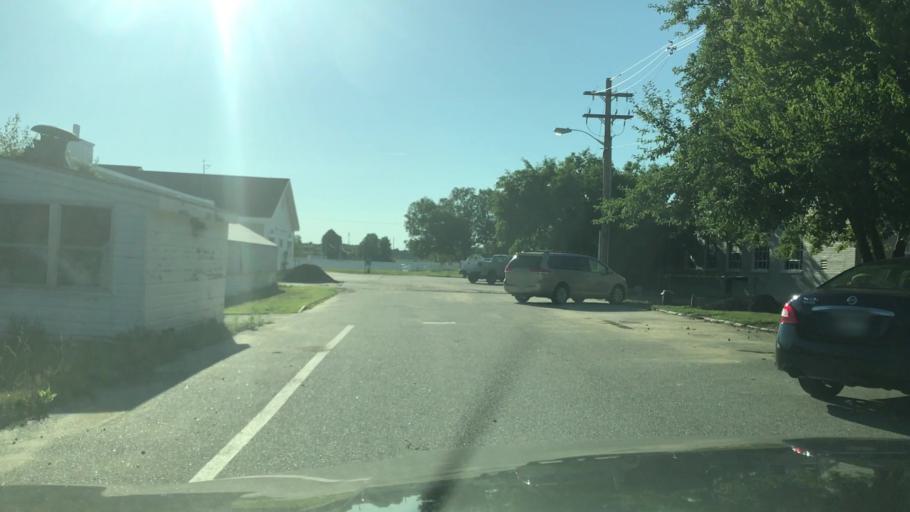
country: US
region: New Hampshire
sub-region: Strafford County
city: Durham
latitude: 43.1409
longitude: -70.9393
